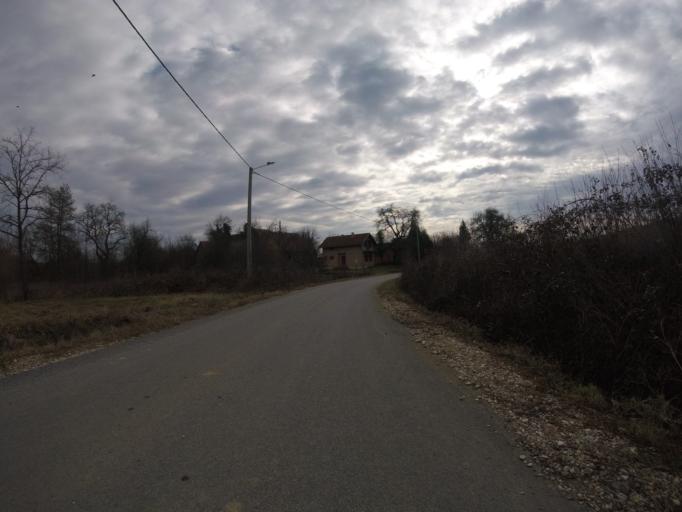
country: HR
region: Sisacko-Moslavacka
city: Glina
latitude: 45.4556
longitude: 16.0627
